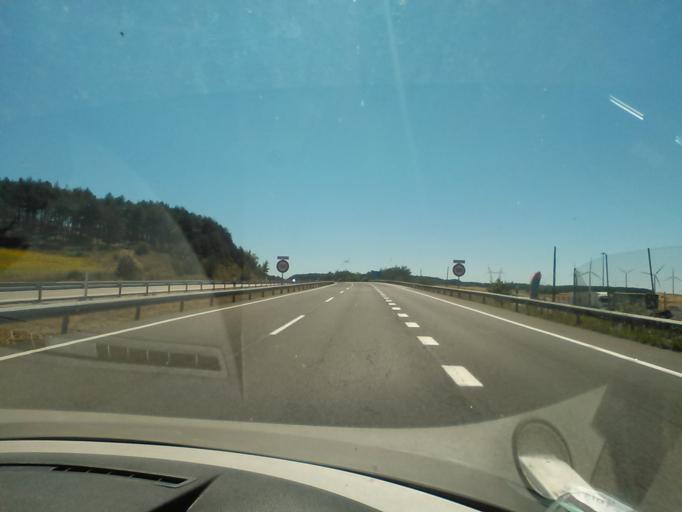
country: ES
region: Castille and Leon
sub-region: Provincia de Burgos
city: Fresno de Rodilla
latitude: 42.4403
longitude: -3.4940
